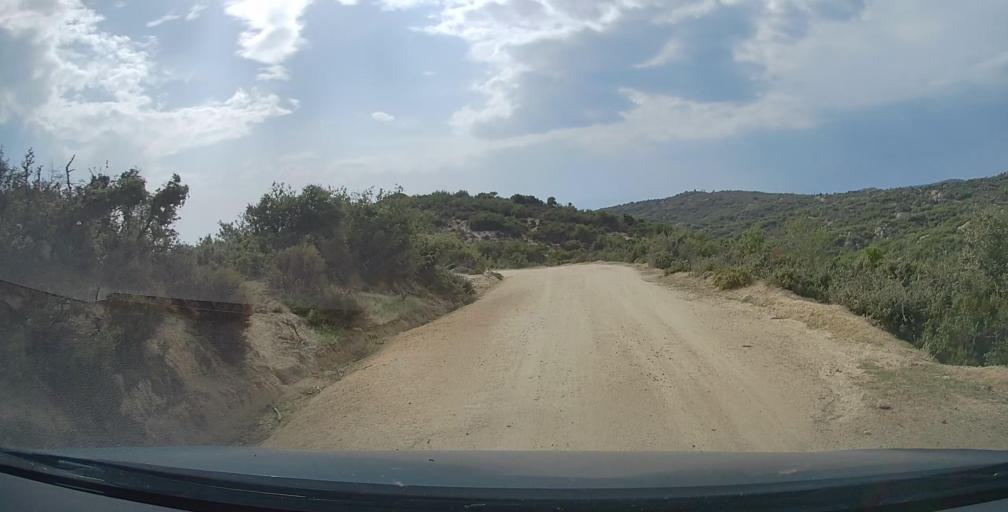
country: GR
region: Central Macedonia
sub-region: Nomos Chalkidikis
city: Sykia
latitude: 39.9968
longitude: 23.9237
